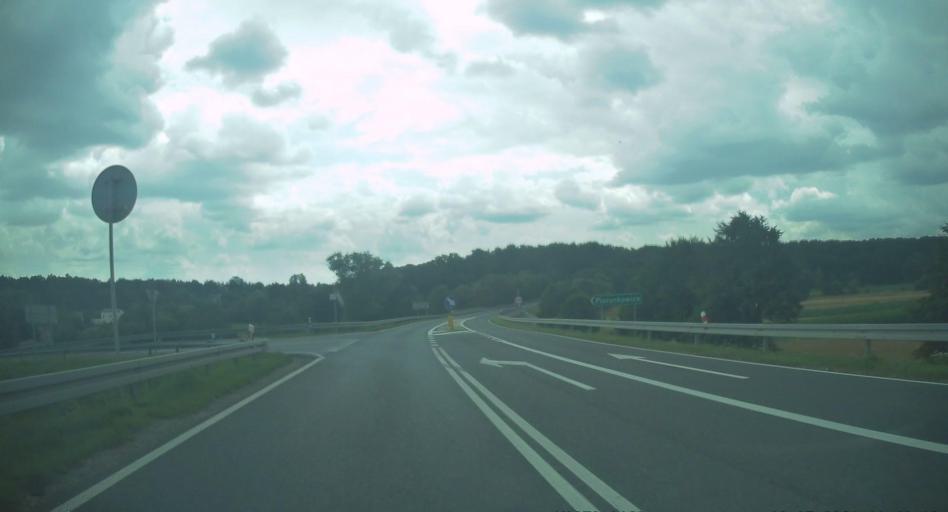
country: PL
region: Opole Voivodeship
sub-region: Powiat prudnicki
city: Laka Prudnicka
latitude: 50.4078
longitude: 17.5083
